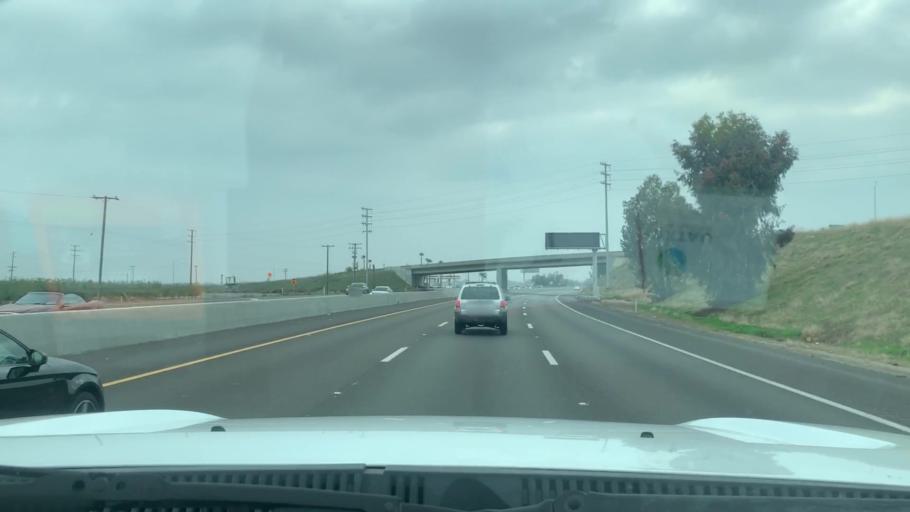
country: US
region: California
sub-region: Tulare County
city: Goshen
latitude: 36.2995
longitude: -119.3857
